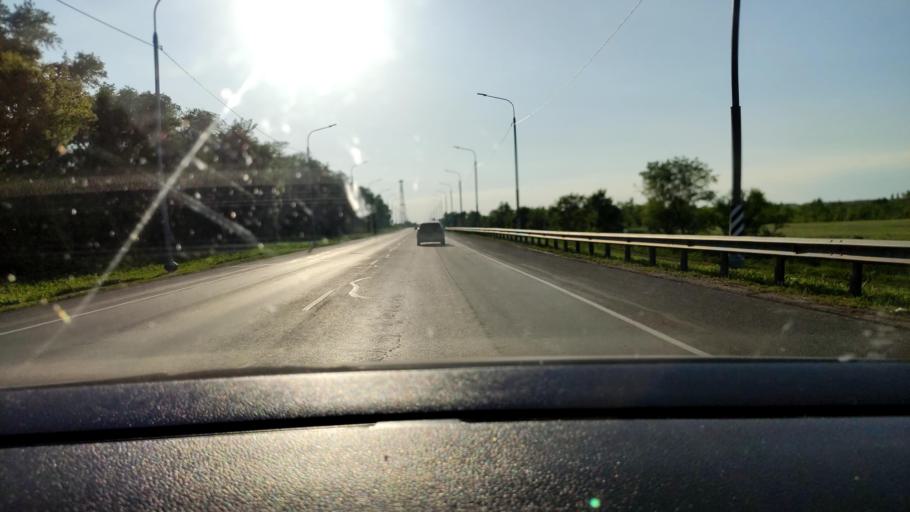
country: RU
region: Voronezj
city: Kashirskoye
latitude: 51.5010
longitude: 39.5779
